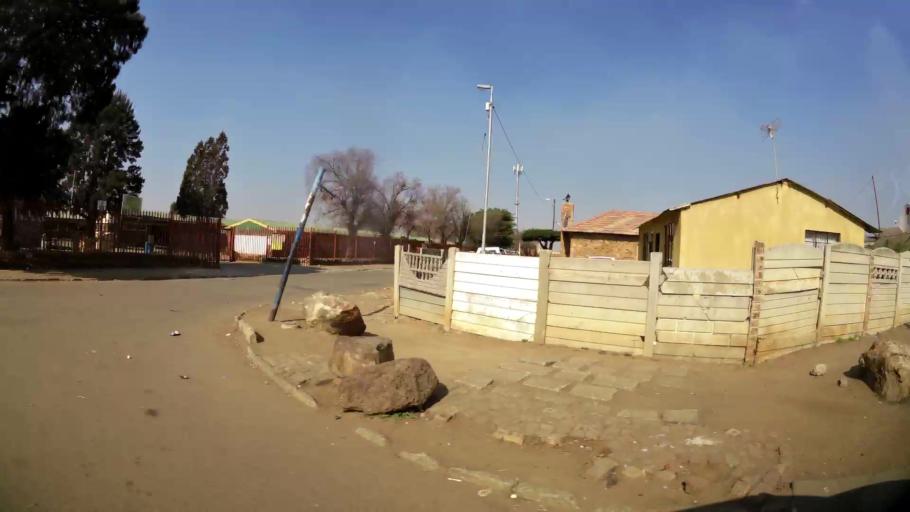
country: ZA
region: Gauteng
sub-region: Ekurhuleni Metropolitan Municipality
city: Brakpan
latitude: -26.1396
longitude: 28.4256
